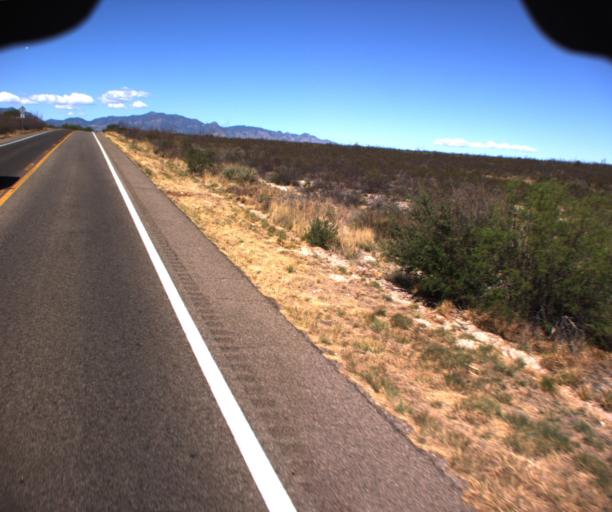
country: US
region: Arizona
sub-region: Cochise County
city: Sierra Vista Southeast
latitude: 31.5475
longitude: -110.1517
